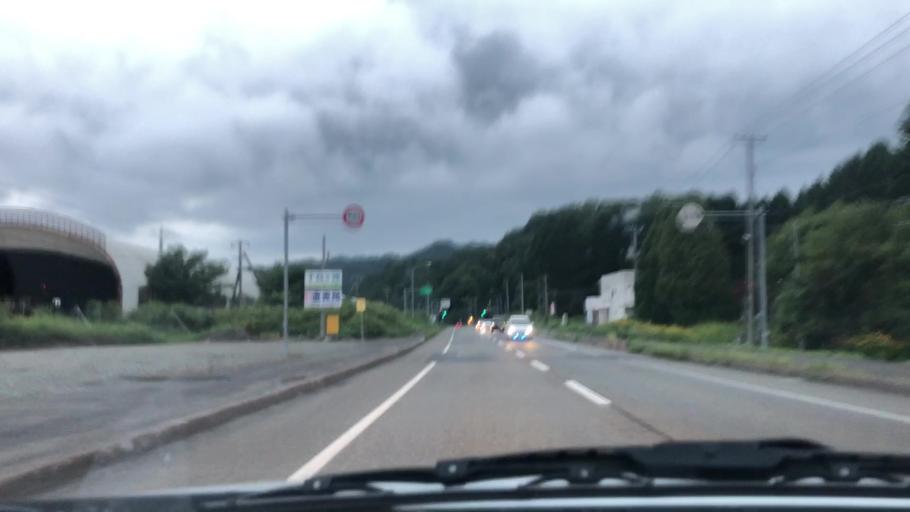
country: JP
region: Hokkaido
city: Chitose
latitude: 42.9110
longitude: 141.9752
